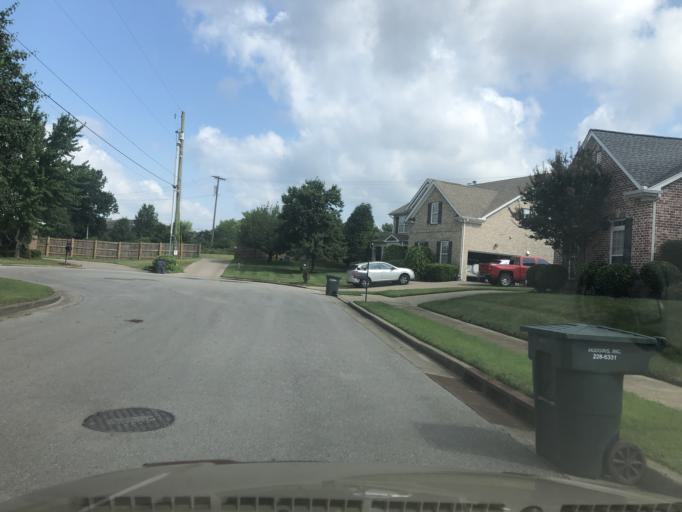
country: US
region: Tennessee
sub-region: Davidson County
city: Lakewood
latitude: 36.2285
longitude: -86.5946
